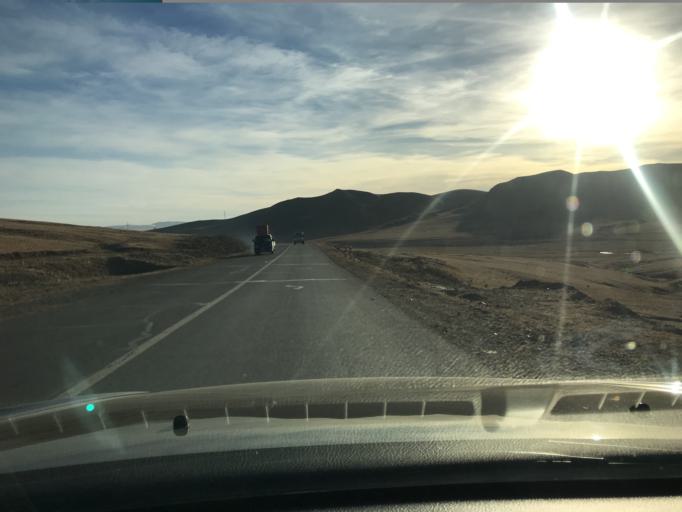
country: MN
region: Central Aimak
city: Dzuunmod
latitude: 47.8076
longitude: 107.3250
